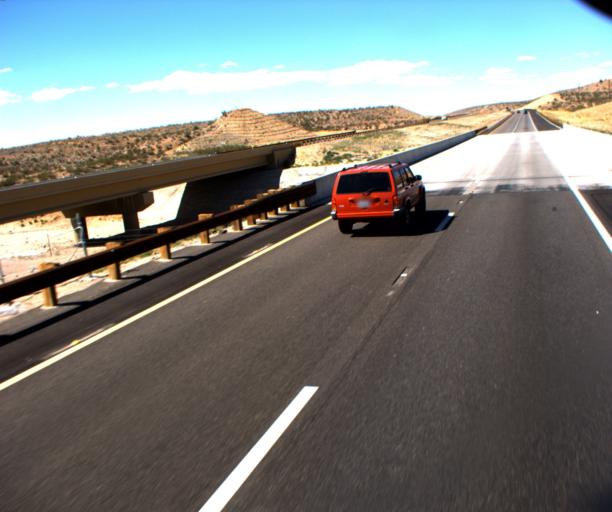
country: US
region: Arizona
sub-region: Mohave County
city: Kingman
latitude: 34.9915
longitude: -113.6655
